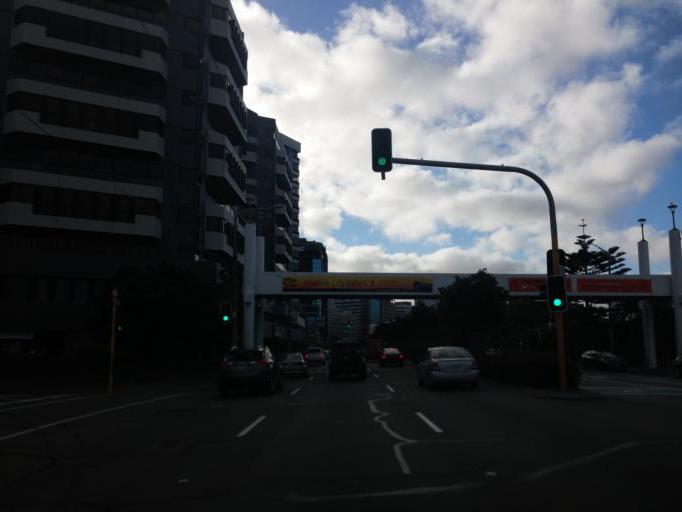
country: NZ
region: Wellington
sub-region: Wellington City
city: Wellington
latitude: -41.2881
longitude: 174.7783
